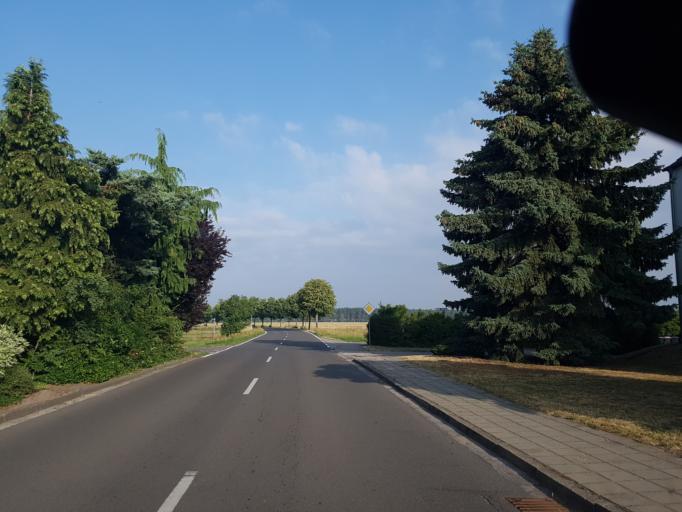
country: DE
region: Saxony-Anhalt
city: Holzdorf
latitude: 51.8551
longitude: 13.0996
